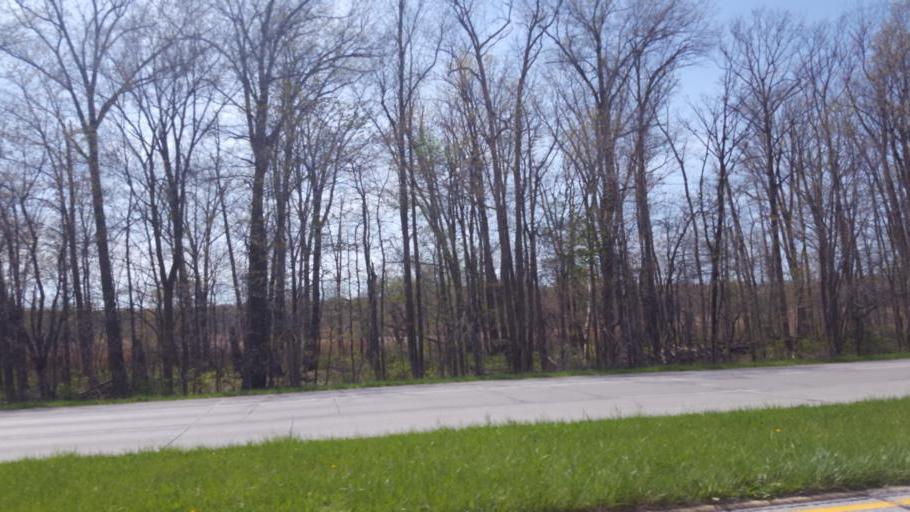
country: US
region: Ohio
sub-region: Lake County
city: Fairport Harbor
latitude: 41.7451
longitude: -81.2876
